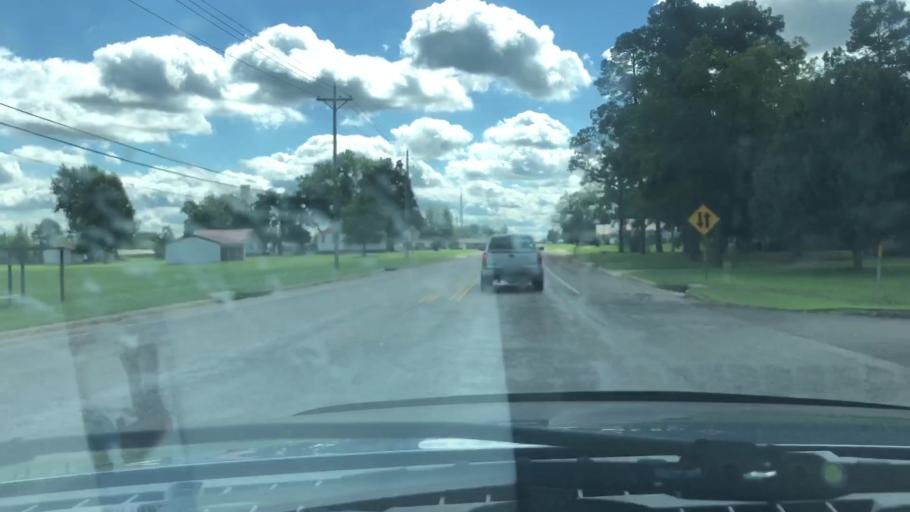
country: US
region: Texas
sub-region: Bowie County
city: Wake Village
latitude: 33.3846
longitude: -94.0921
